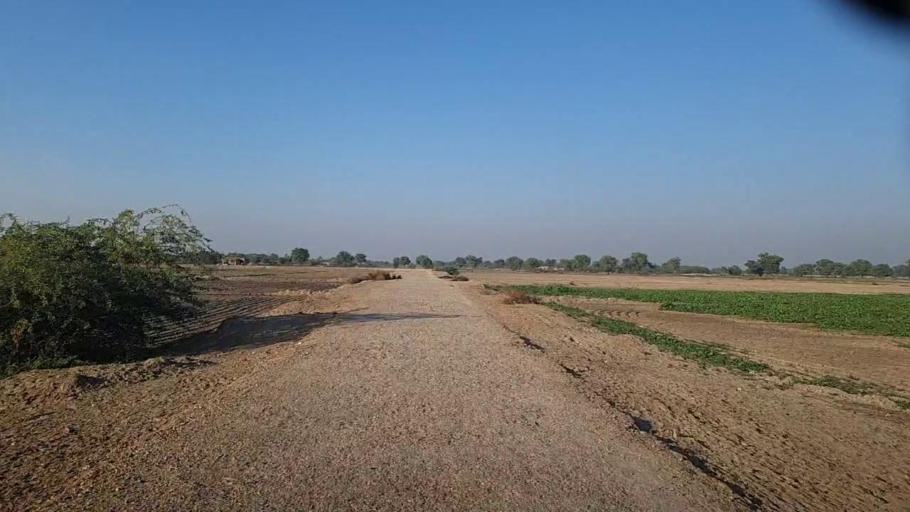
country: PK
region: Sindh
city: Pad Idan
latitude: 26.7319
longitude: 68.3492
